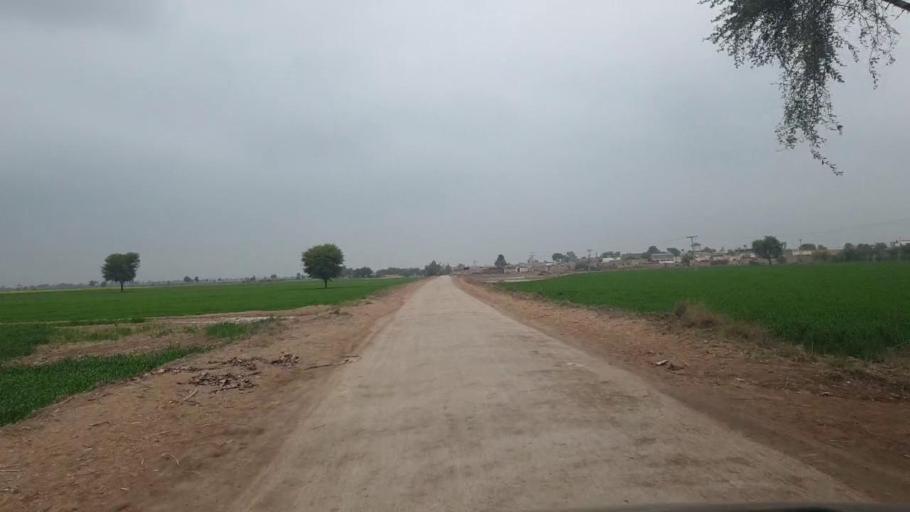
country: PK
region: Sindh
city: Shahdadpur
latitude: 25.9458
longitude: 68.7245
